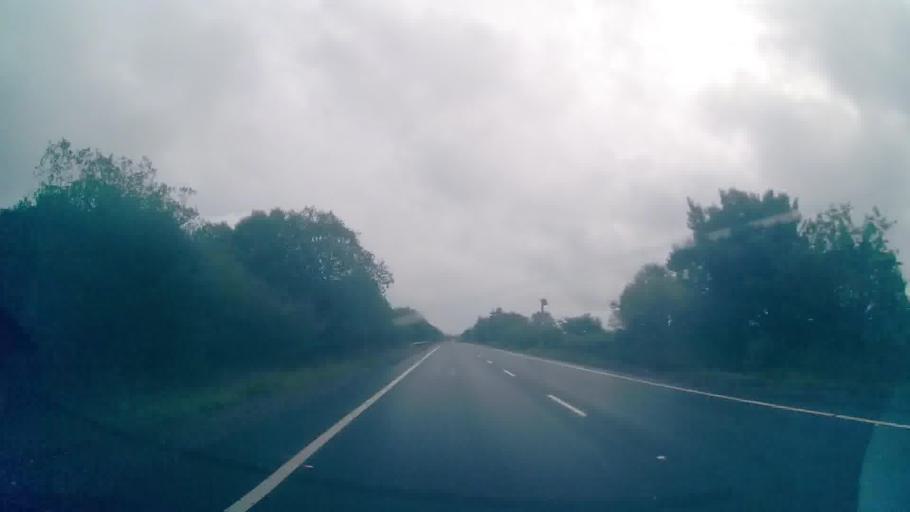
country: GB
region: Scotland
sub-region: Dumfries and Galloway
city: Locharbriggs
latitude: 55.0833
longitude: -3.5851
